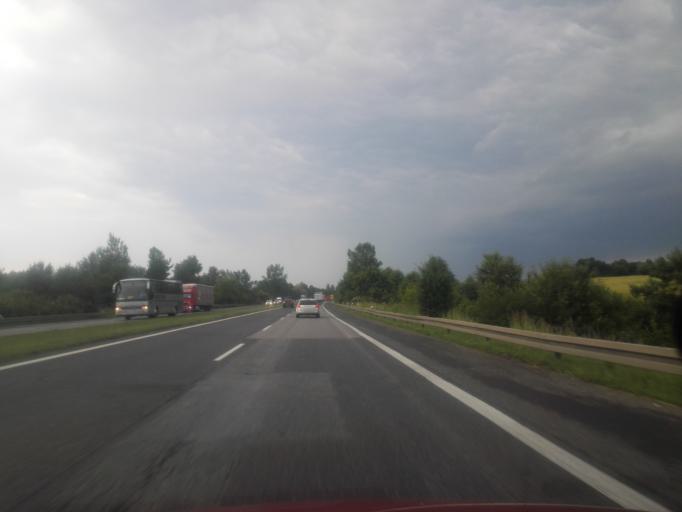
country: PL
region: Silesian Voivodeship
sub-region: Powiat czestochowski
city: Redziny
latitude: 50.8648
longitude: 19.1549
